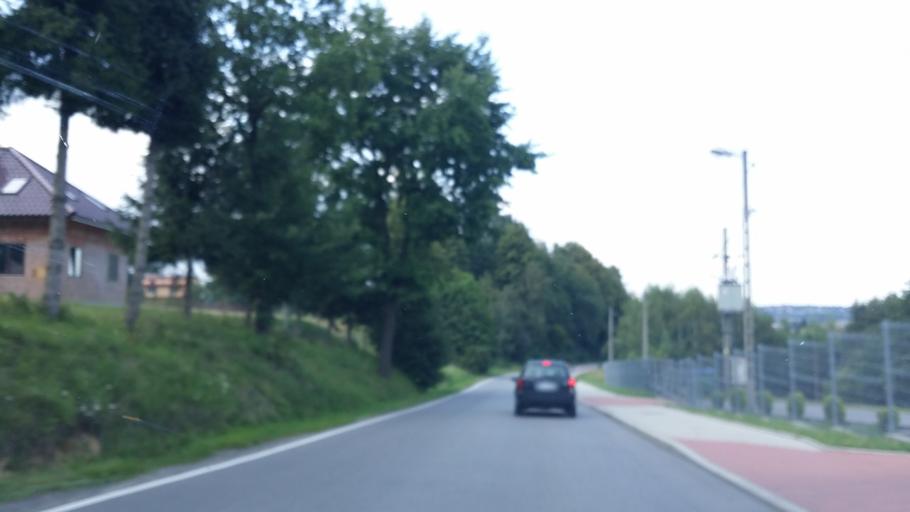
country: PL
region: Lesser Poland Voivodeship
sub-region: Powiat wielicki
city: Pawlikowice
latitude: 49.9339
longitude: 20.0297
